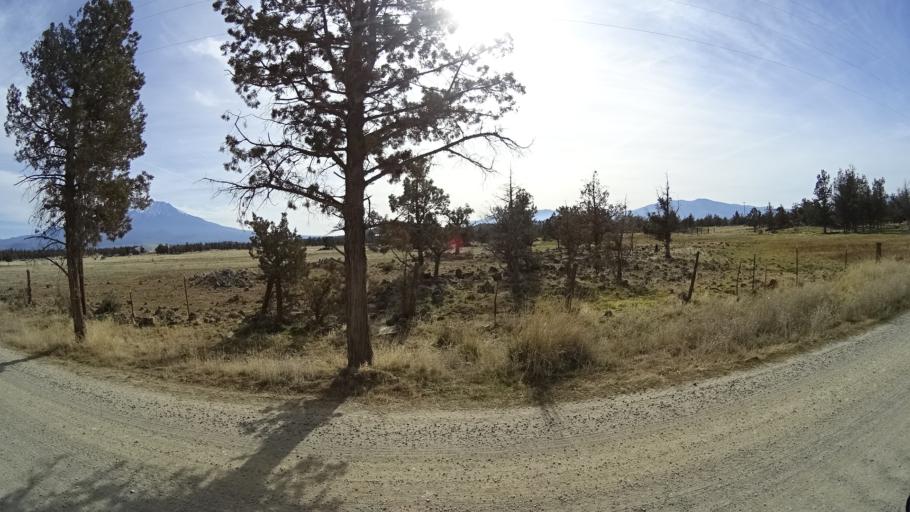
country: US
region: California
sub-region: Siskiyou County
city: Weed
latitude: 41.5955
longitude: -122.4069
